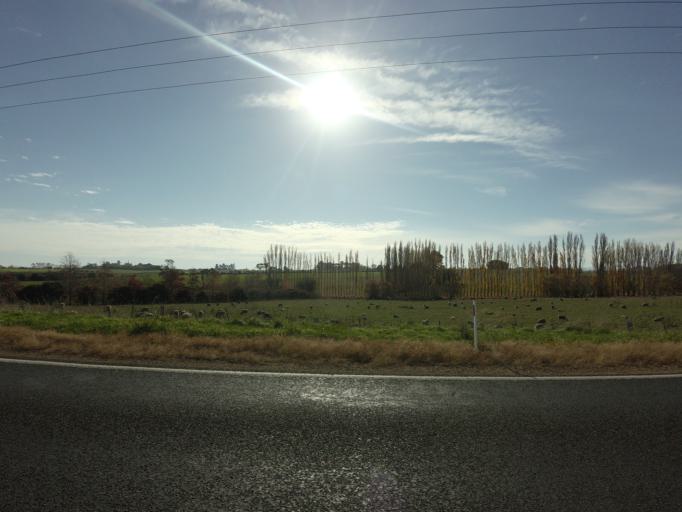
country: AU
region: Tasmania
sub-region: Meander Valley
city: Westbury
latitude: -41.5298
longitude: 146.9210
